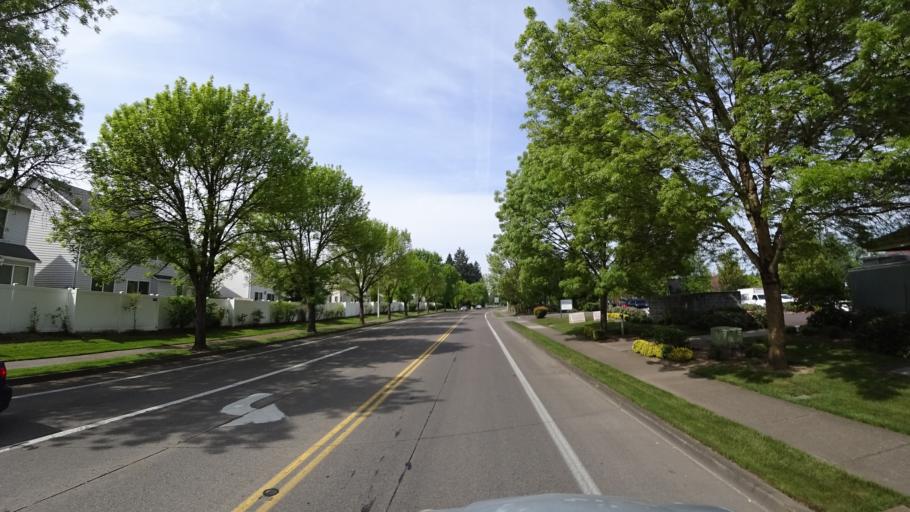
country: US
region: Oregon
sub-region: Washington County
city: Rockcreek
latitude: 45.5202
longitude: -122.9290
